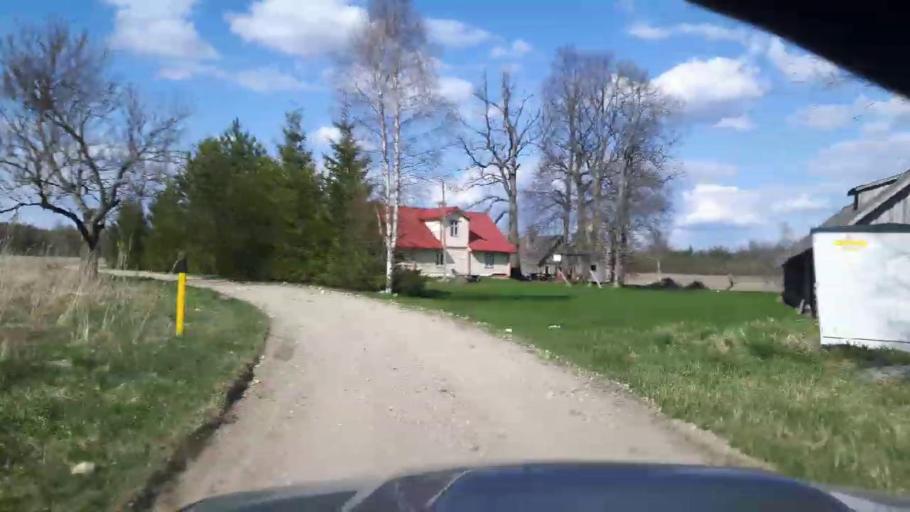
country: EE
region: Paernumaa
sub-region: Tootsi vald
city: Tootsi
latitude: 58.4379
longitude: 24.8724
